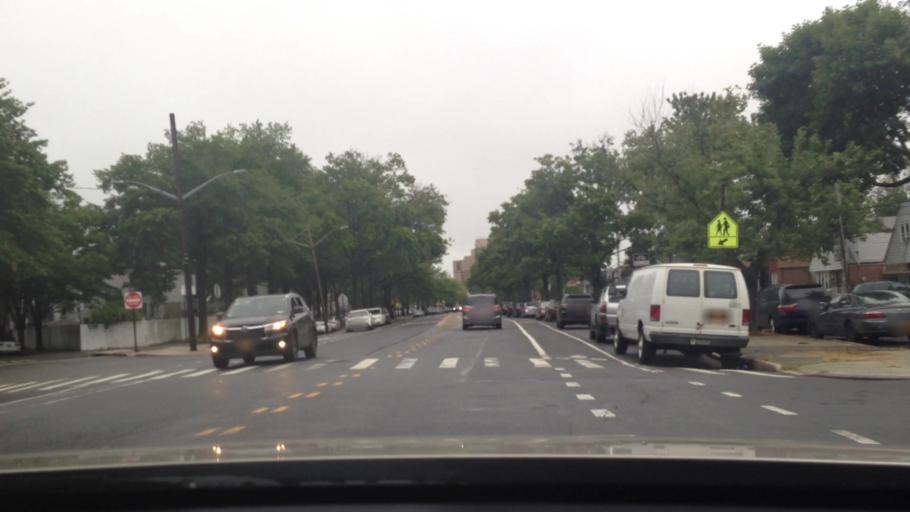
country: US
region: New York
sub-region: Nassau County
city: Bellerose Terrace
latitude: 40.7311
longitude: -73.7363
